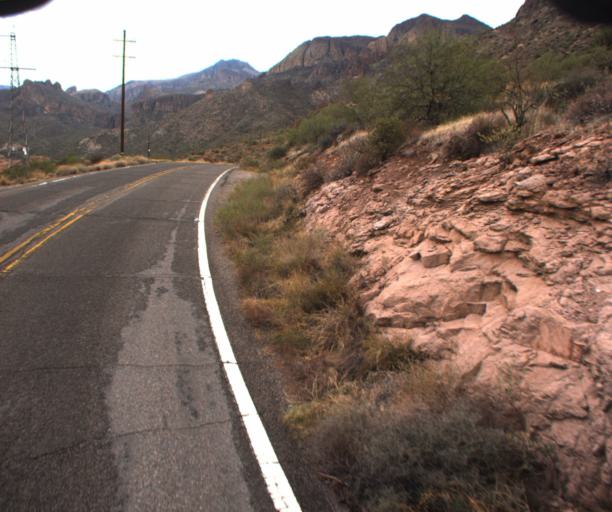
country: US
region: Arizona
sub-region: Pinal County
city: Apache Junction
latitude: 33.5293
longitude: -111.4027
